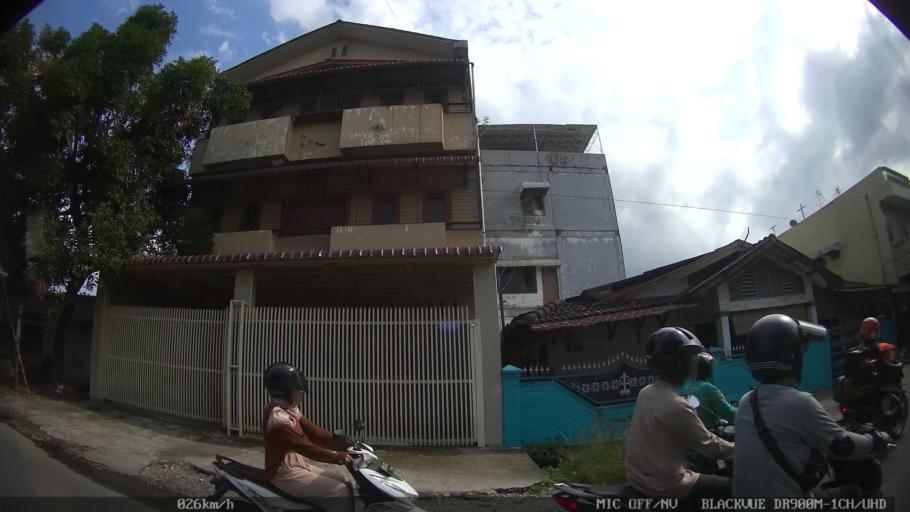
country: ID
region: North Sumatra
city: Medan
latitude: 3.6207
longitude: 98.6659
